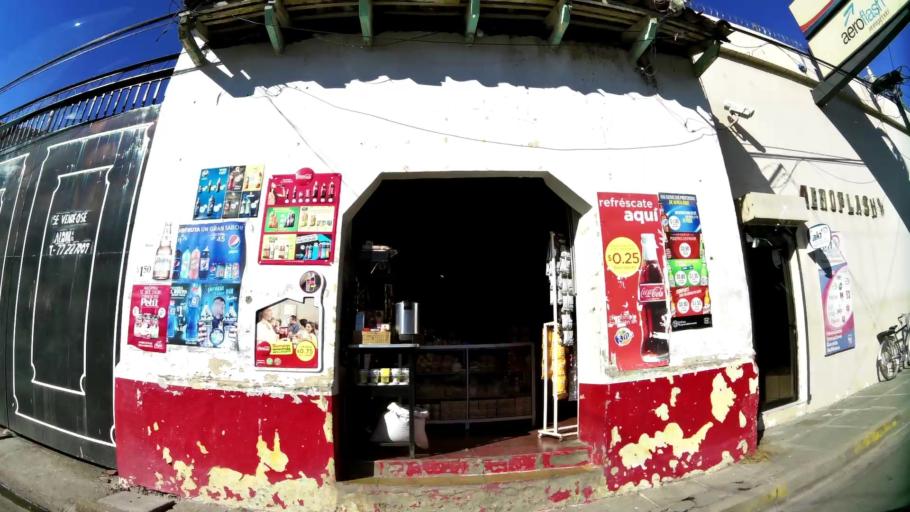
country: SV
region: San Miguel
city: San Miguel
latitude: 13.4765
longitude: -88.1777
